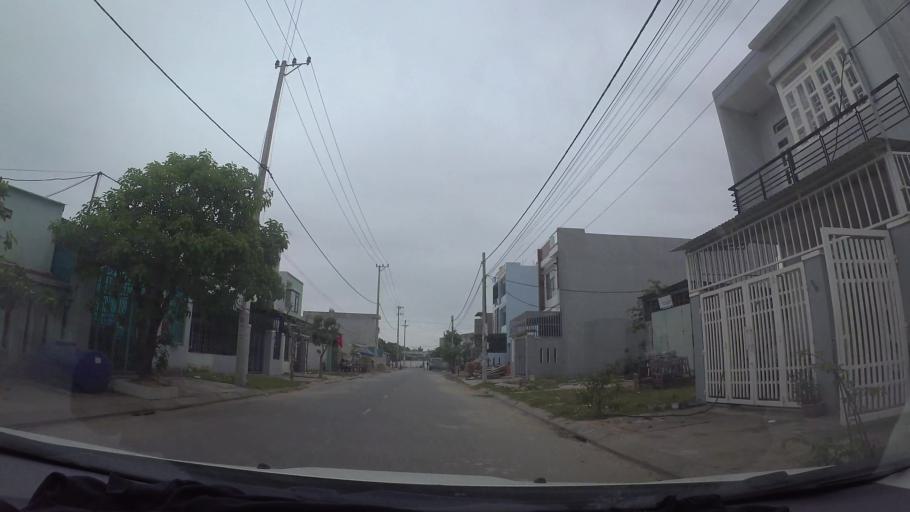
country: VN
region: Da Nang
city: Lien Chieu
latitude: 16.0696
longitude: 108.1408
